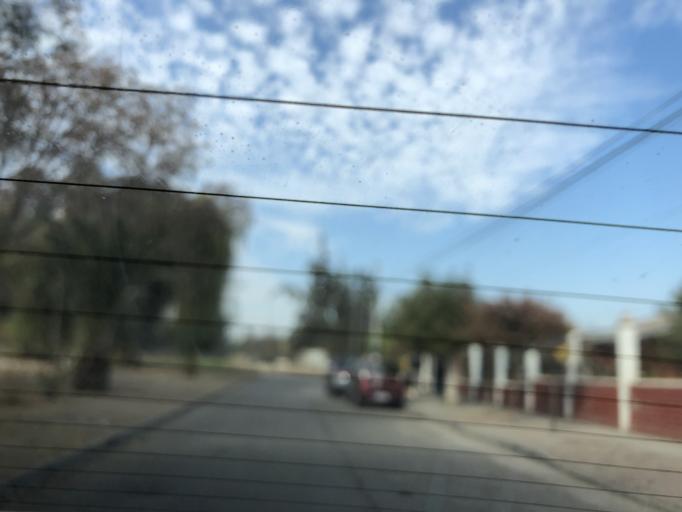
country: CL
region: Santiago Metropolitan
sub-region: Provincia de Cordillera
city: Puente Alto
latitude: -33.5765
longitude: -70.5522
